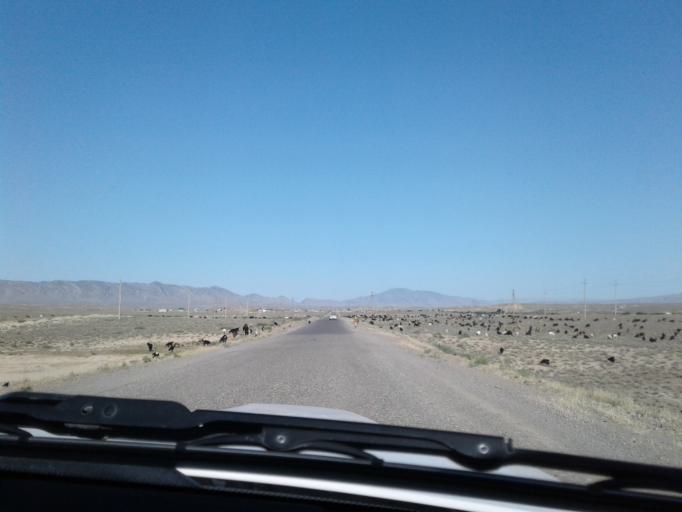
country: TM
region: Balkan
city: Magtymguly
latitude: 38.6861
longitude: 56.4370
